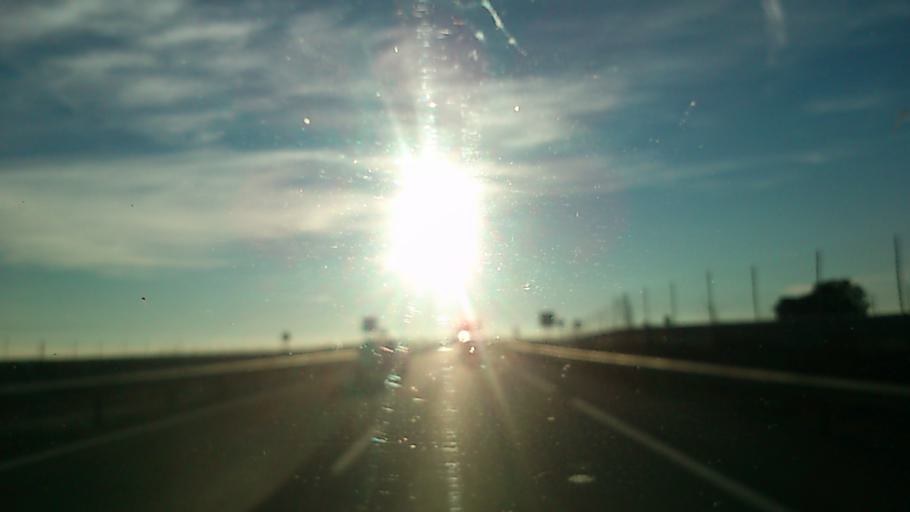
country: ES
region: Castille-La Mancha
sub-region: Provincia de Guadalajara
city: Muduex
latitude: 40.8112
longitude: -2.9390
